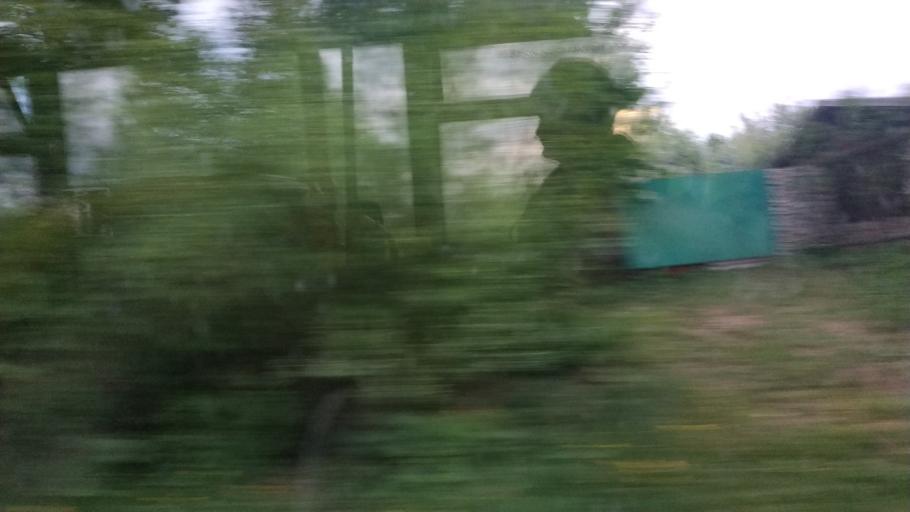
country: RU
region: Moskovskaya
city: Kashira
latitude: 54.8524
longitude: 38.1759
